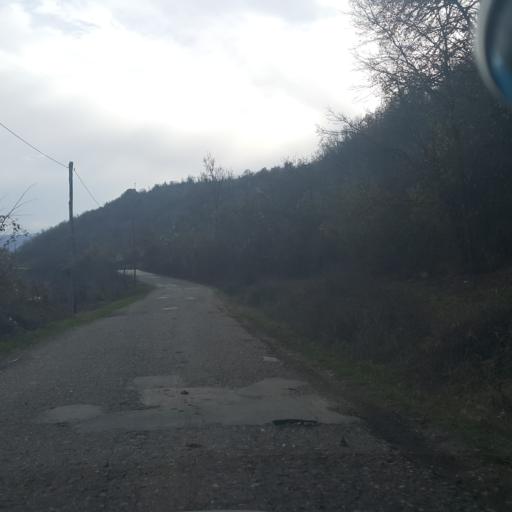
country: RS
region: Central Serbia
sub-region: Zajecarski Okrug
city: Knjazevac
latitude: 43.6069
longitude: 22.2581
